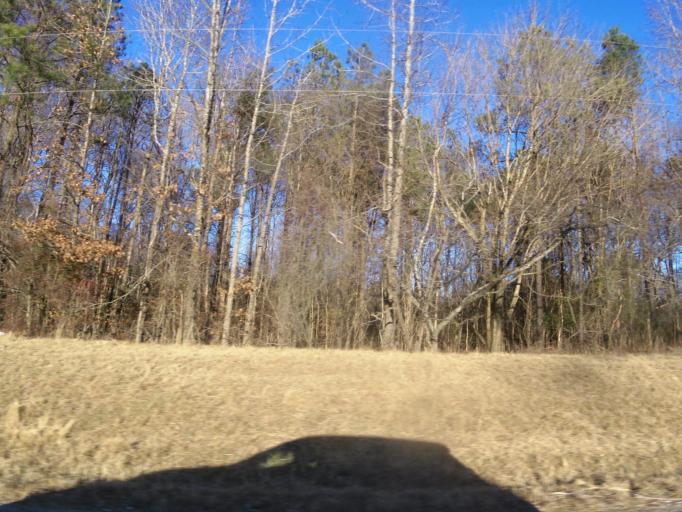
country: US
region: Virginia
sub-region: City of Franklin
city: Franklin
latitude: 36.6745
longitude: -76.8993
